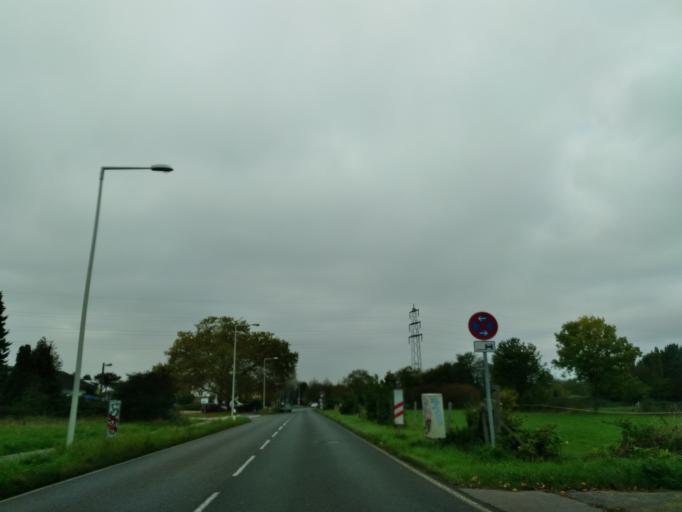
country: DE
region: North Rhine-Westphalia
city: Sankt Augustin
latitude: 50.7459
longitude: 7.1644
